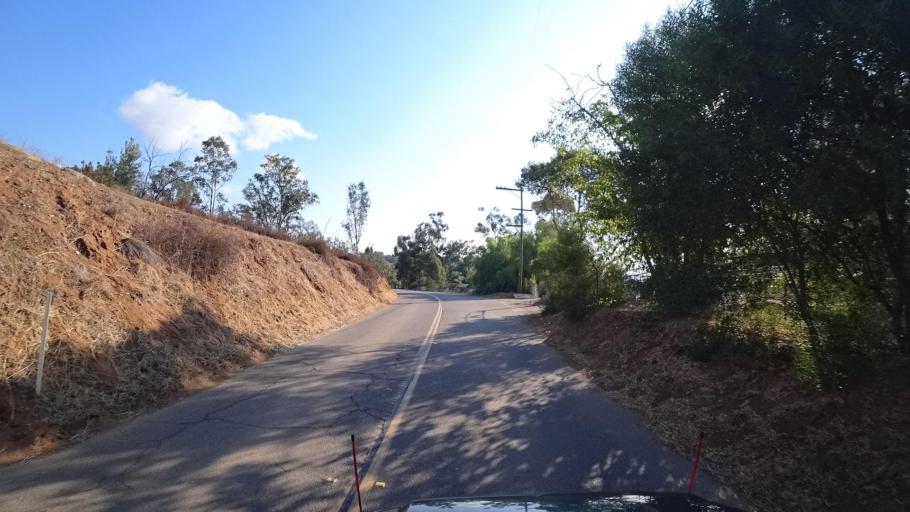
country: US
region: California
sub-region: San Diego County
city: Eucalyptus Hills
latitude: 32.8867
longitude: -116.9517
